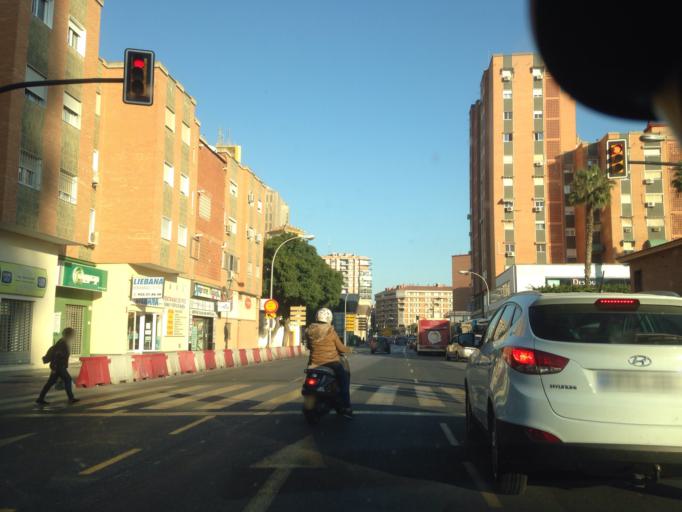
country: ES
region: Andalusia
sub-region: Provincia de Malaga
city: Malaga
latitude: 36.7159
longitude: -4.4293
